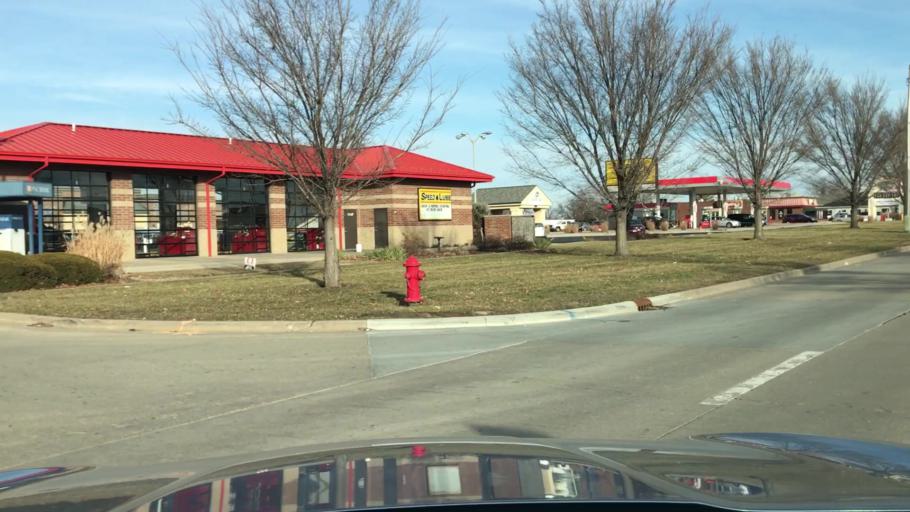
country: US
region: Illinois
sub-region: McLean County
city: Normal
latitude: 40.5104
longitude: -88.9571
